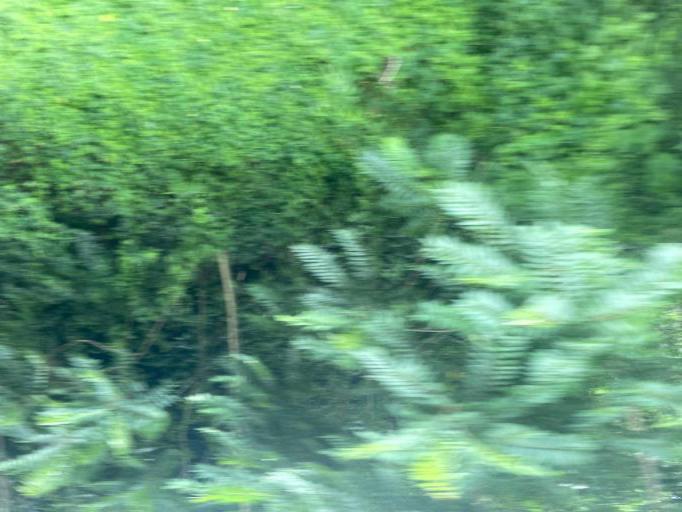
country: JP
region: Gunma
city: Shibukawa
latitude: 36.5508
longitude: 139.0359
